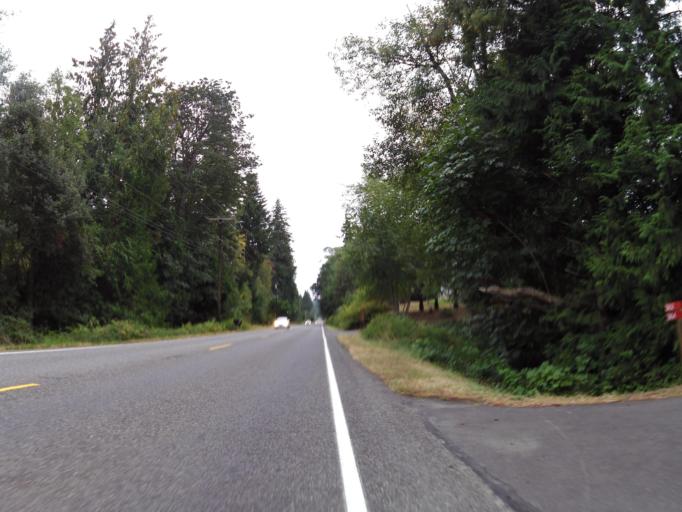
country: US
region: Washington
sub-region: Jefferson County
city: Port Hadlock-Irondale
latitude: 47.9972
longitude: -122.7235
